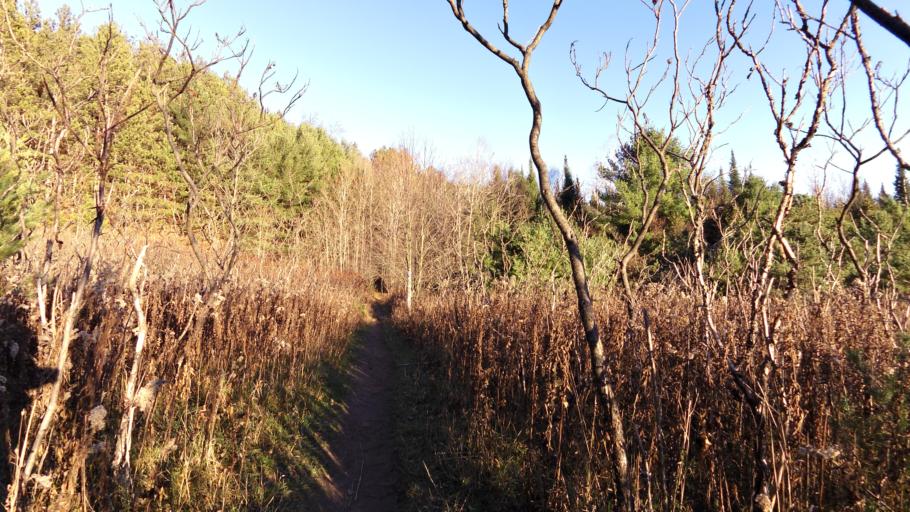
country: CA
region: Ontario
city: Orangeville
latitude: 43.9898
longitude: -80.0534
